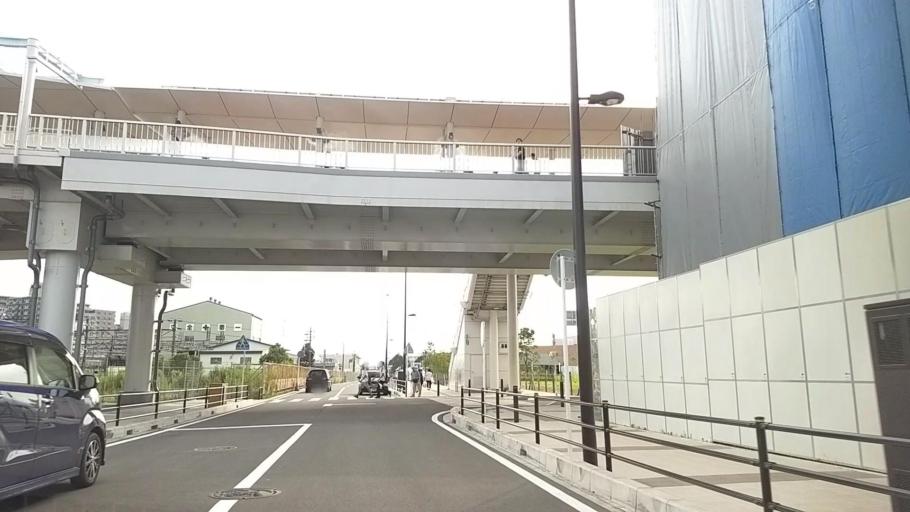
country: JP
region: Kanagawa
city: Atsugi
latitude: 35.4535
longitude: 139.3906
